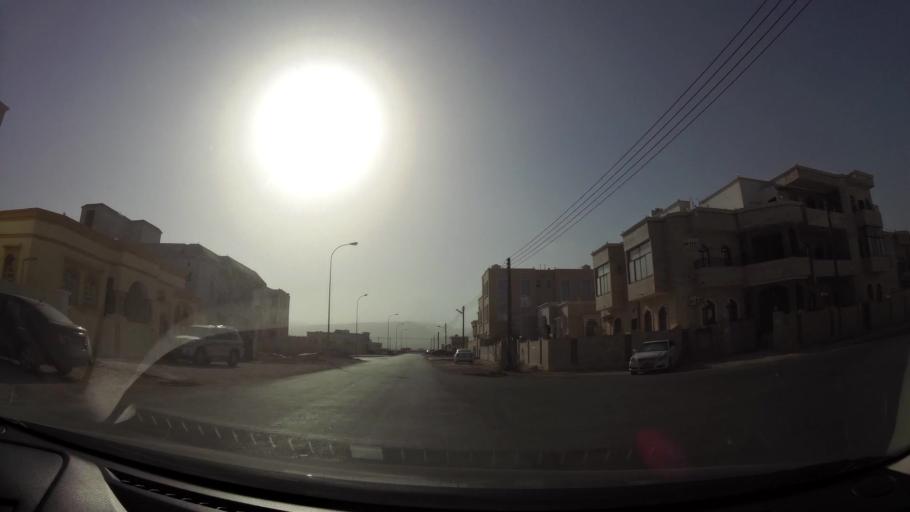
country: OM
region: Zufar
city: Salalah
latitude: 17.0162
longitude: 54.0128
